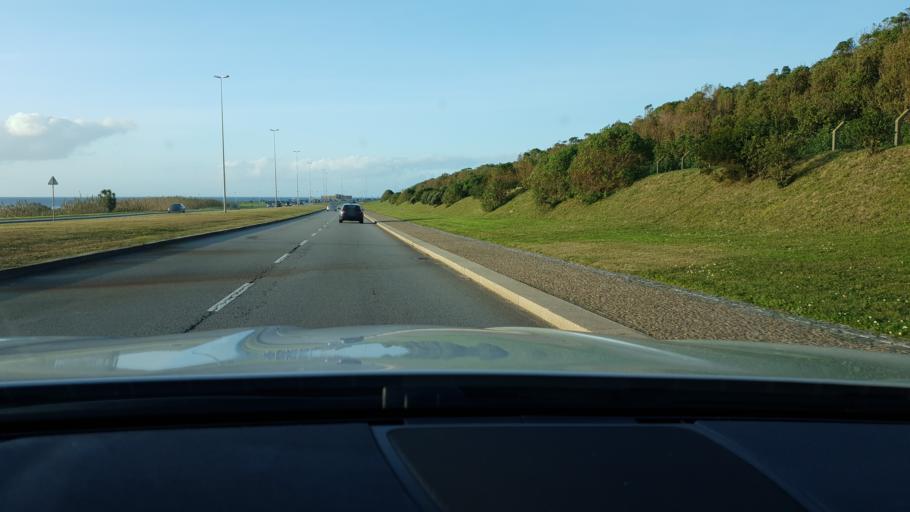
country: PT
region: Porto
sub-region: Matosinhos
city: Leca da Palmeira
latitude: 41.2030
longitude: -8.7123
